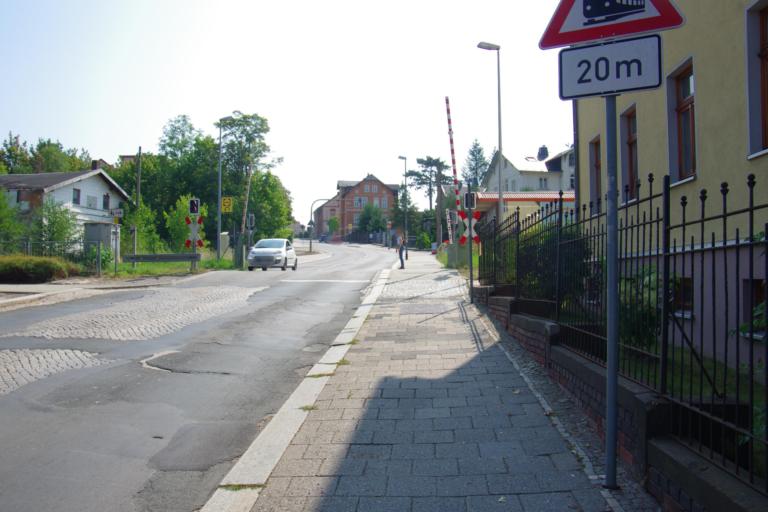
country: DE
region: Saxony
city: Frankenberg
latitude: 50.9098
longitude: 13.0408
